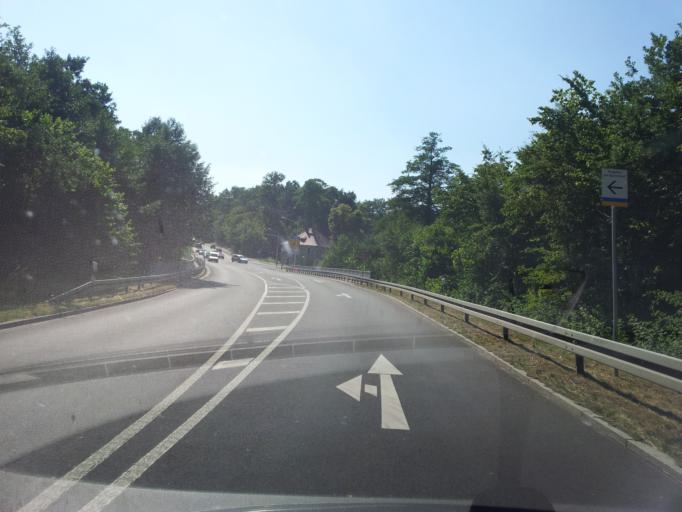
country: DE
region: Saxony
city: Konigsbruck
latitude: 51.2615
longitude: 13.9040
